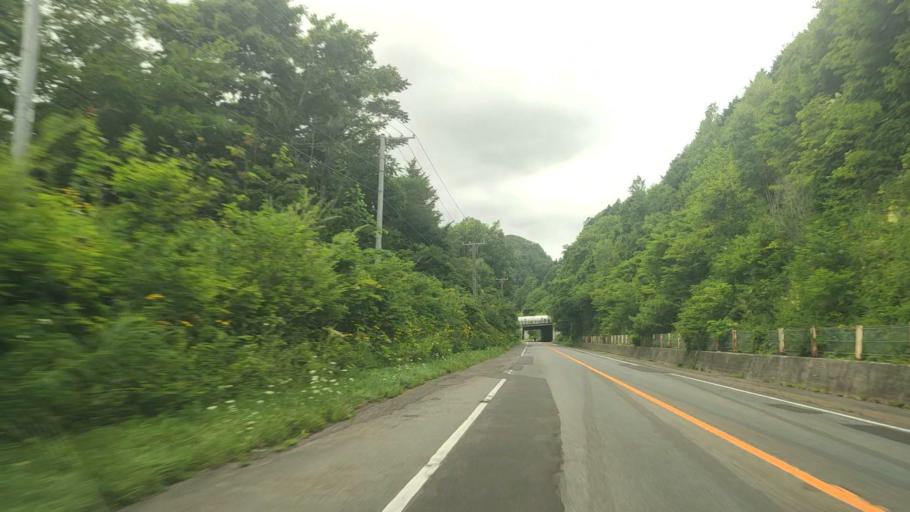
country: JP
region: Hokkaido
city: Niseko Town
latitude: 42.5997
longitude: 140.5735
